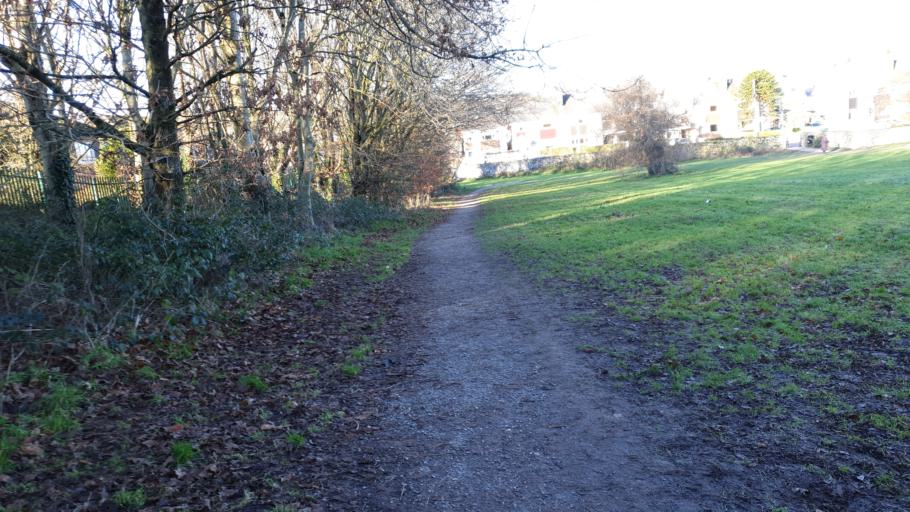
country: IE
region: Munster
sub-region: County Cork
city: Cork
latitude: 51.8865
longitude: -8.4241
